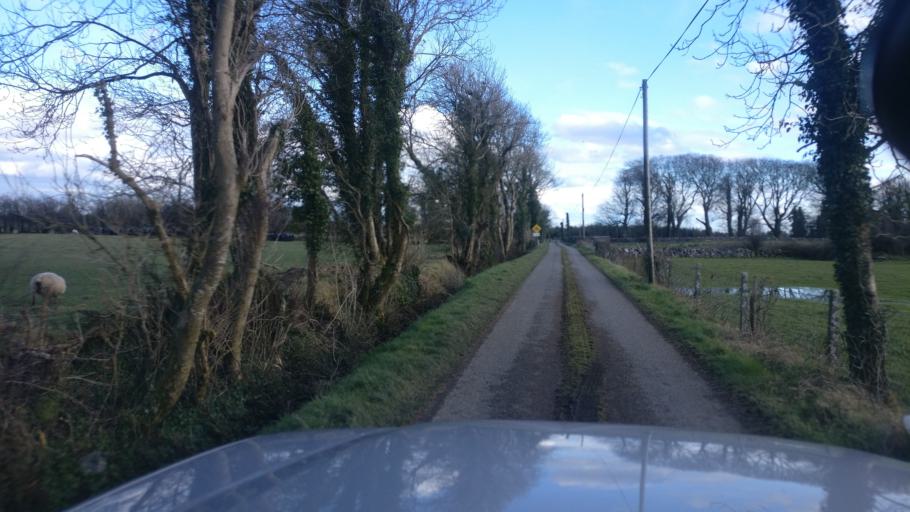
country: IE
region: Connaught
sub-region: County Galway
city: Loughrea
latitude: 53.2142
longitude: -8.4069
